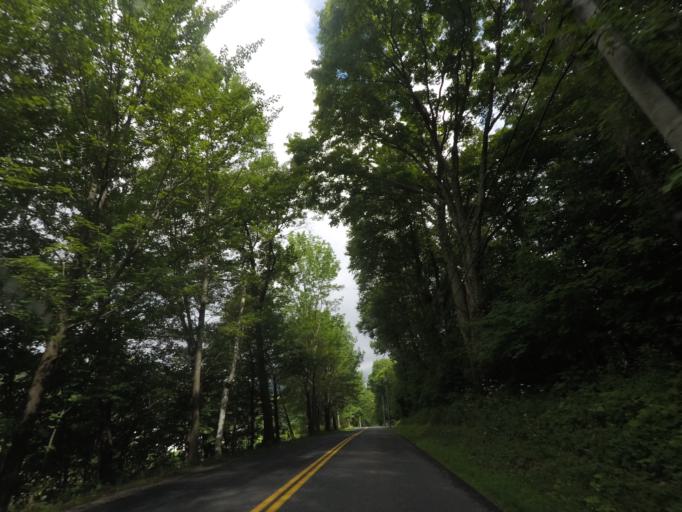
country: US
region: Massachusetts
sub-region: Berkshire County
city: Lanesborough
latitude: 42.5540
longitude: -73.2504
